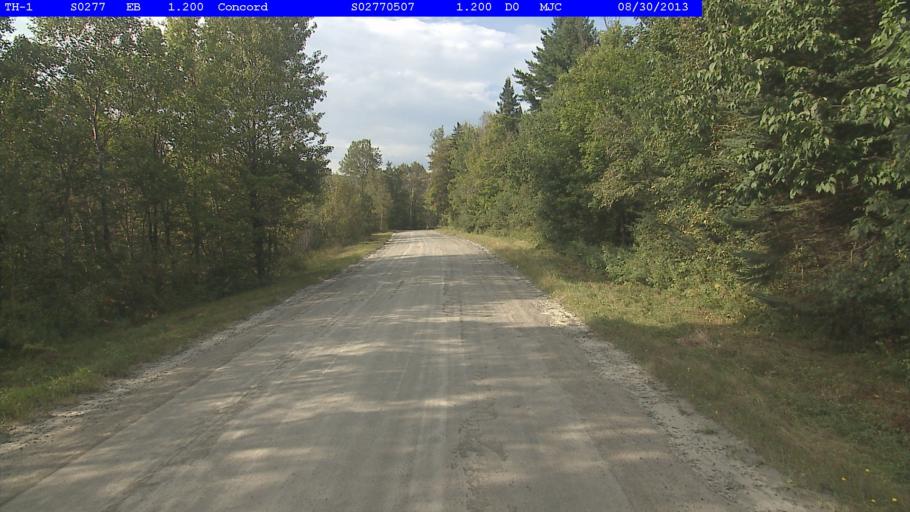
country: US
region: Vermont
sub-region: Caledonia County
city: Lyndonville
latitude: 44.4807
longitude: -71.8639
